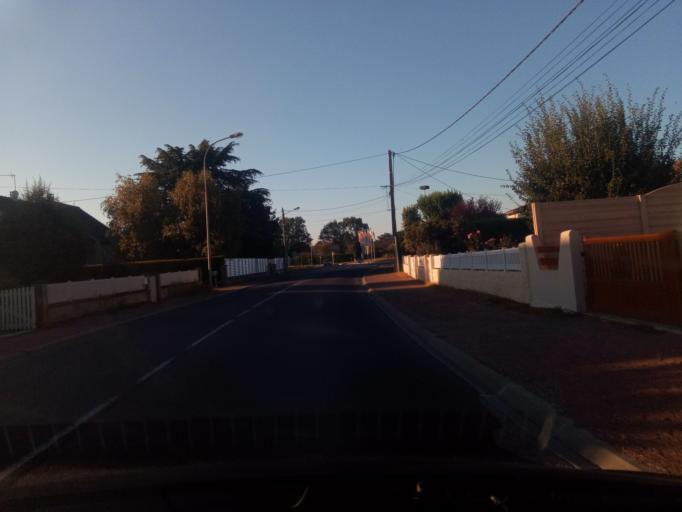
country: FR
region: Poitou-Charentes
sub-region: Departement de la Vienne
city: Montmorillon
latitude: 46.4255
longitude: 0.8592
